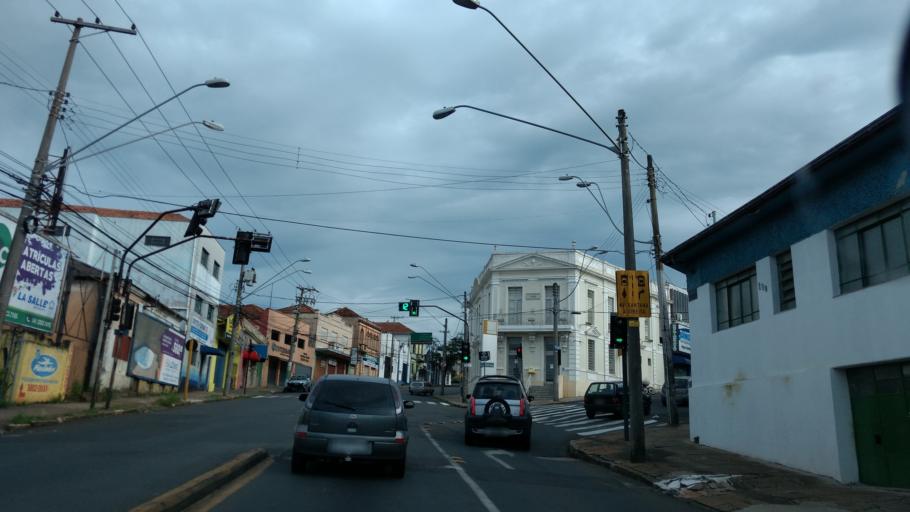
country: BR
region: Sao Paulo
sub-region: Botucatu
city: Botucatu
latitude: -22.8770
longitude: -48.4435
